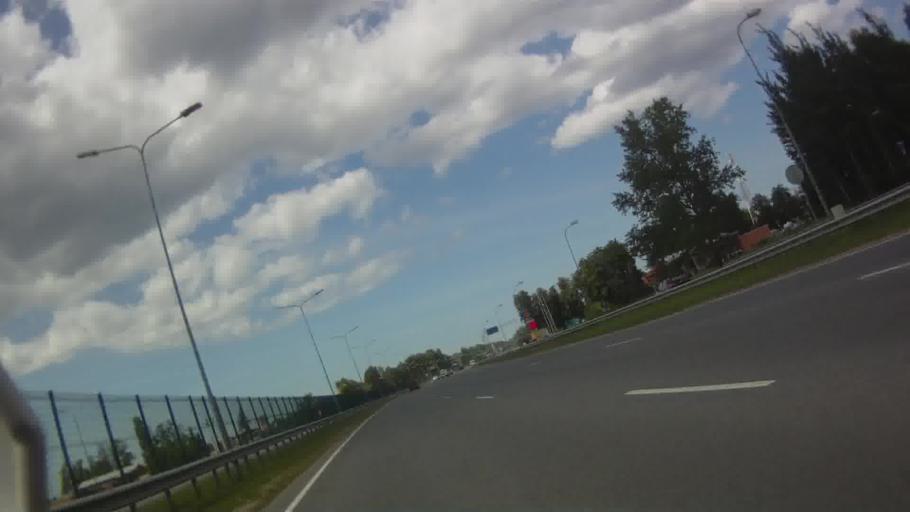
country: LV
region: Marupe
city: Marupe
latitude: 56.9328
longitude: 24.0068
